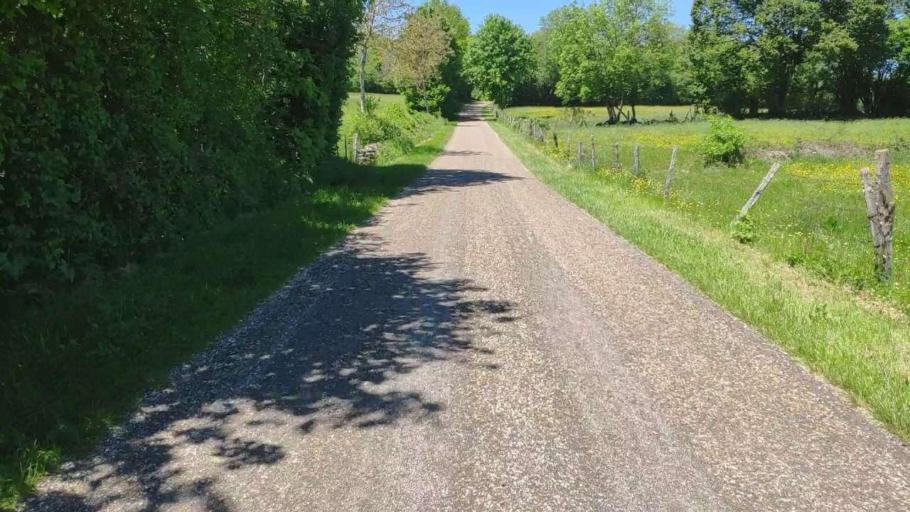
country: FR
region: Franche-Comte
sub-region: Departement du Jura
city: Poligny
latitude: 46.7386
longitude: 5.6794
